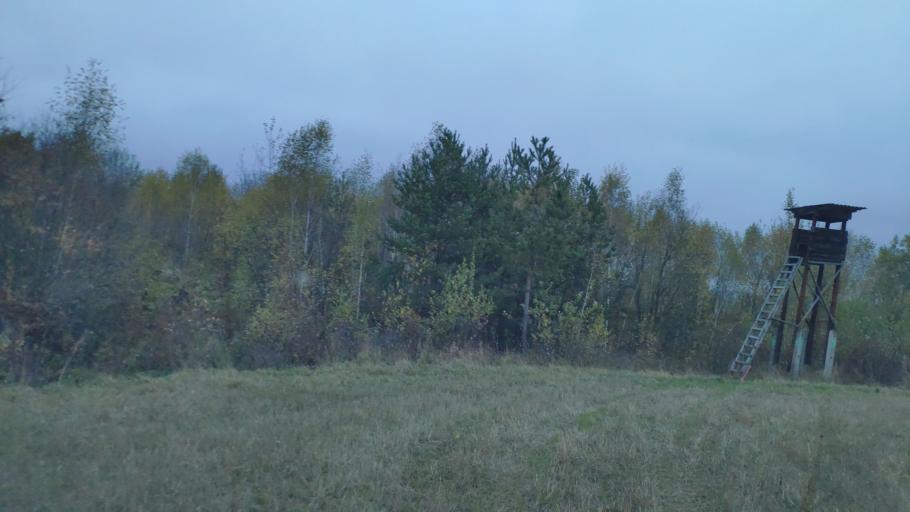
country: SK
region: Presovsky
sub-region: Okres Presov
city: Presov
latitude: 48.9342
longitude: 21.0852
